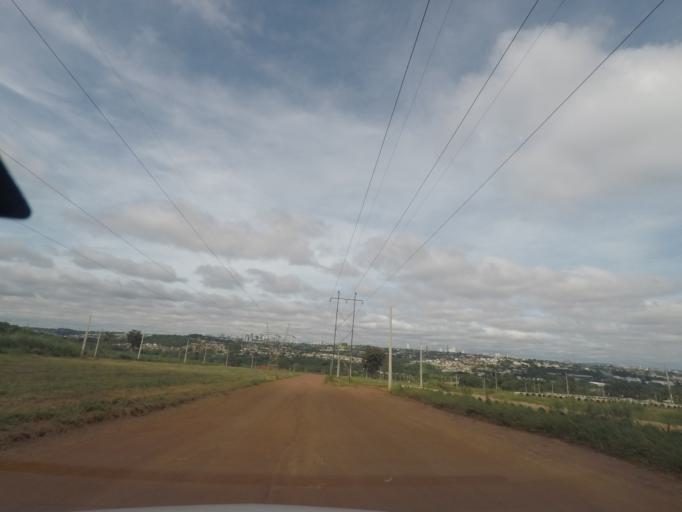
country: BR
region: Goias
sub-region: Goiania
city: Goiania
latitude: -16.6743
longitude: -49.1889
